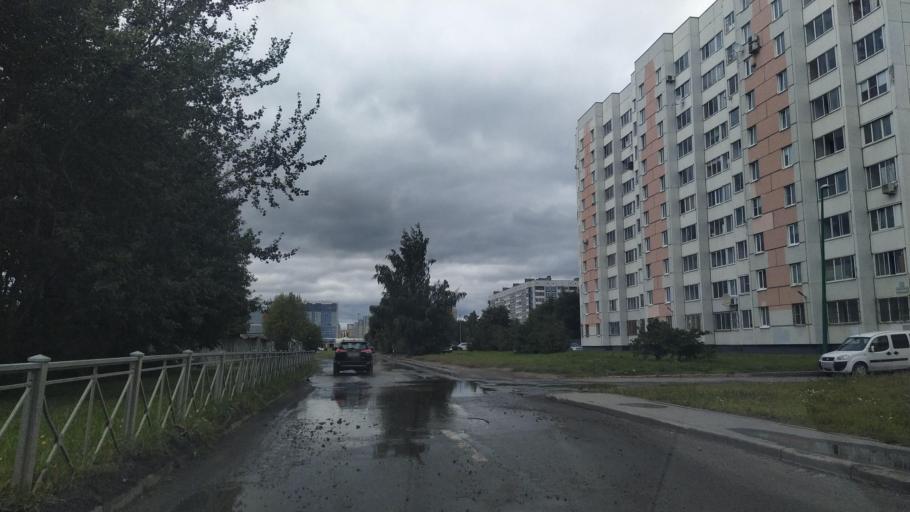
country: RU
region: St.-Petersburg
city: Staraya Derevnya
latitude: 59.9987
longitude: 30.2421
